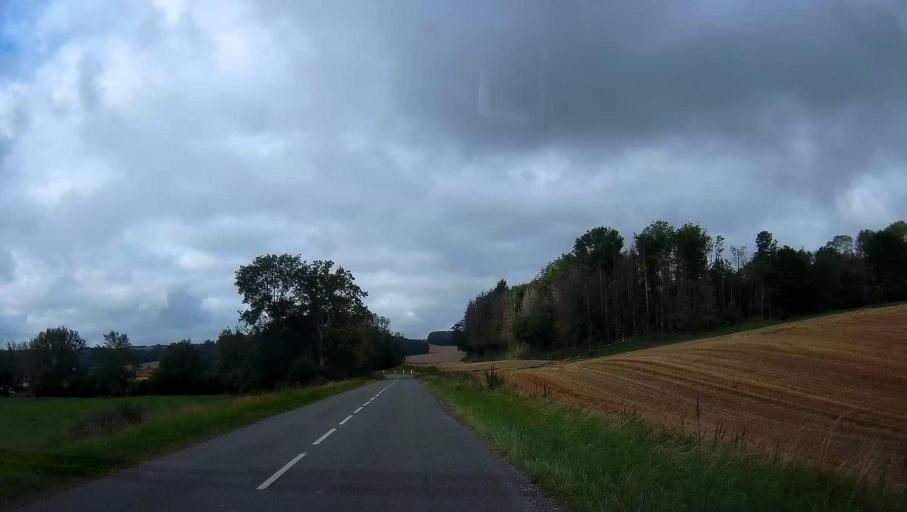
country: FR
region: Champagne-Ardenne
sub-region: Departement des Ardennes
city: Chateau-Porcien
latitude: 49.6434
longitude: 4.2474
